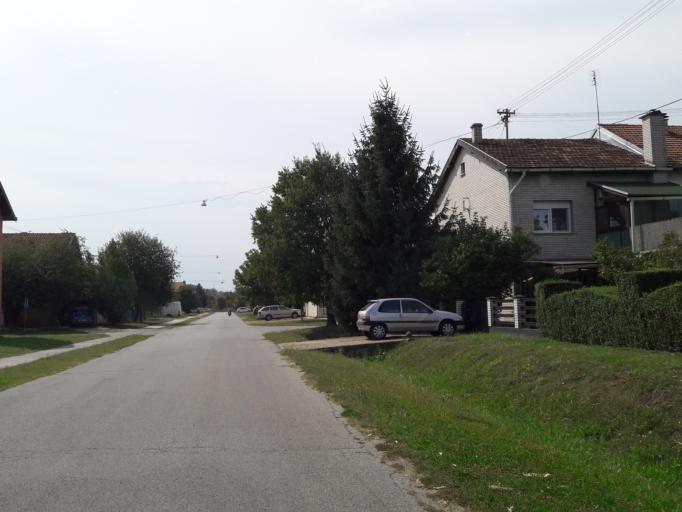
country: HR
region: Osjecko-Baranjska
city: Visnjevac
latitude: 45.5330
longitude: 18.6238
